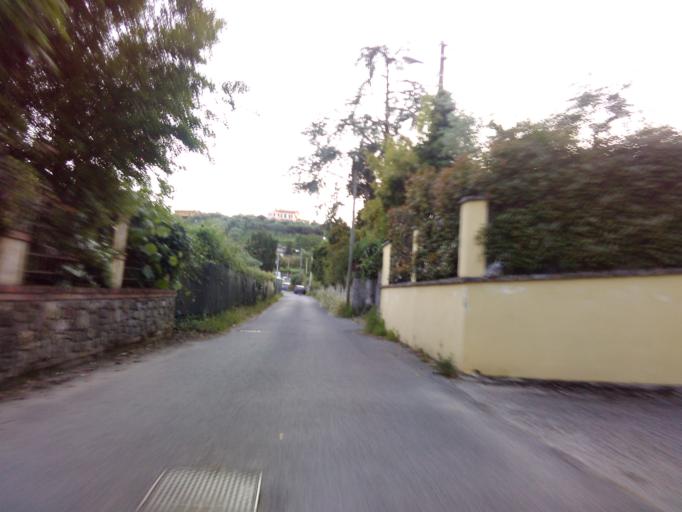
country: IT
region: Tuscany
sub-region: Provincia di Massa-Carrara
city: Massa
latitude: 44.0423
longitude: 10.1012
